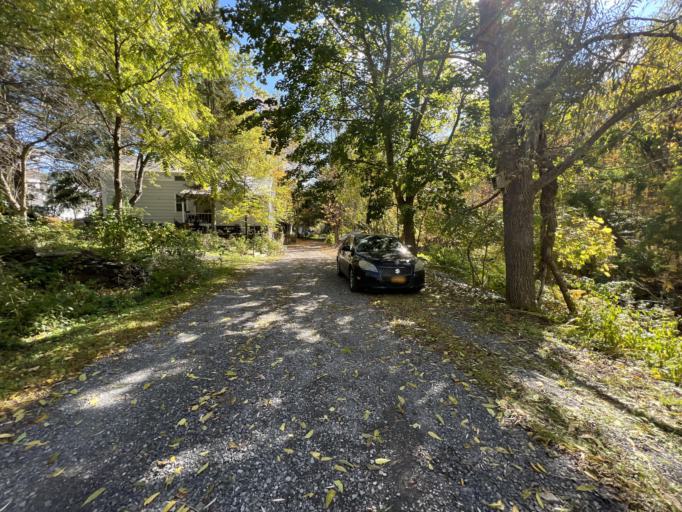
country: US
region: New York
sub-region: Albany County
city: Altamont
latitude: 42.5153
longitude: -74.1365
